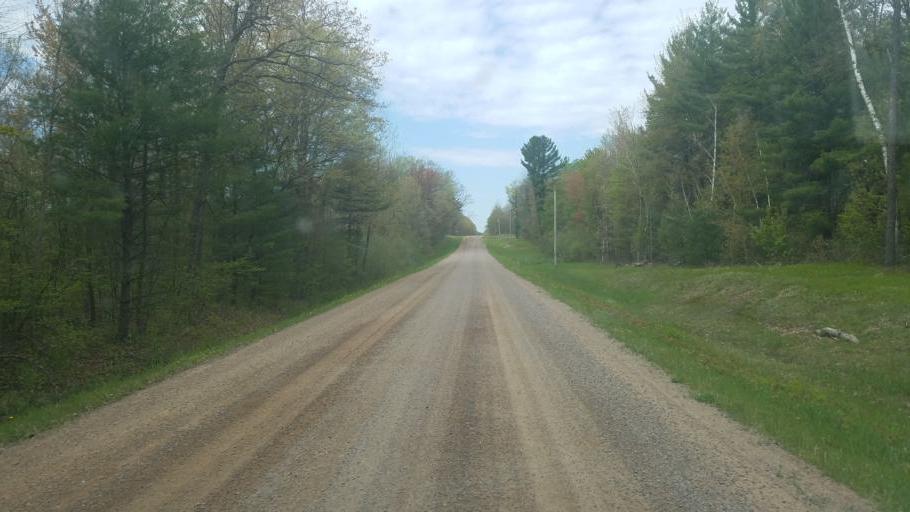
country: US
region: Wisconsin
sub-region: Clark County
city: Neillsville
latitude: 44.4660
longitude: -90.4930
